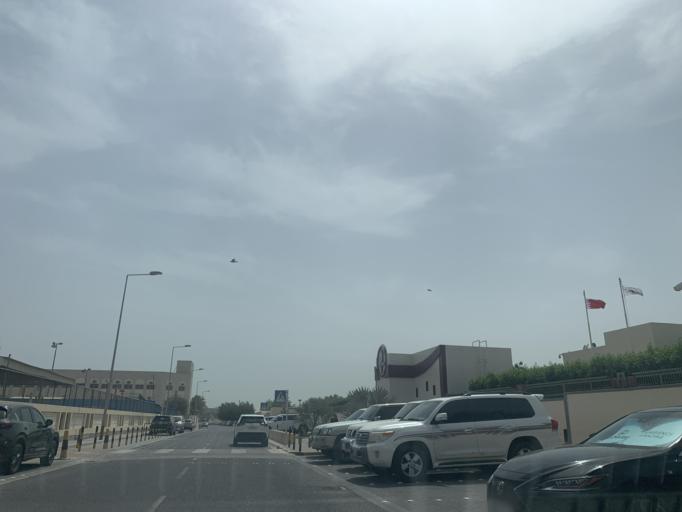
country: BH
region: Northern
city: Madinat `Isa
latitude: 26.1591
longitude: 50.5497
